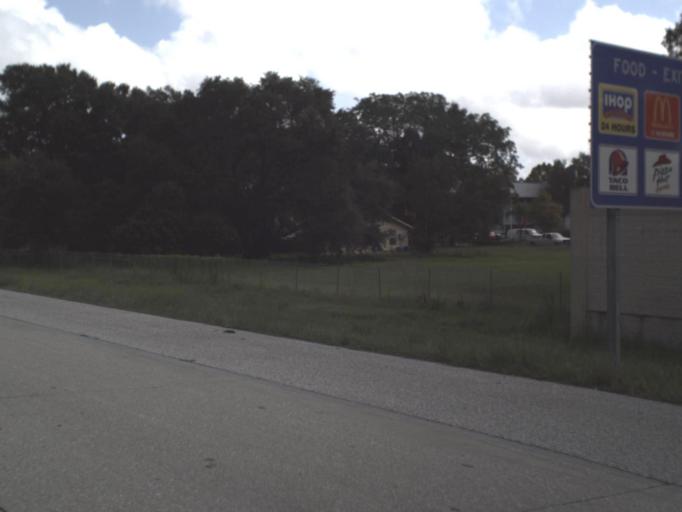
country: US
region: Florida
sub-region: Hillsborough County
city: Lake Magdalene
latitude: 28.0730
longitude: -82.4546
